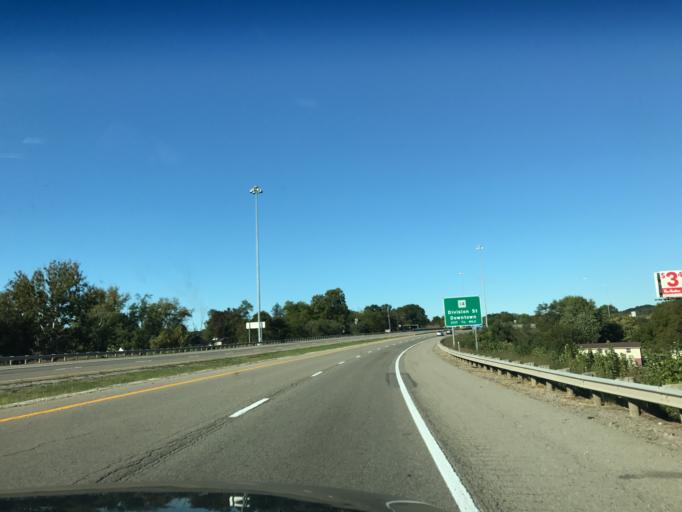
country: US
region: West Virginia
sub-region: Wood County
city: Parkersburg
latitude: 39.2545
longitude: -81.5380
